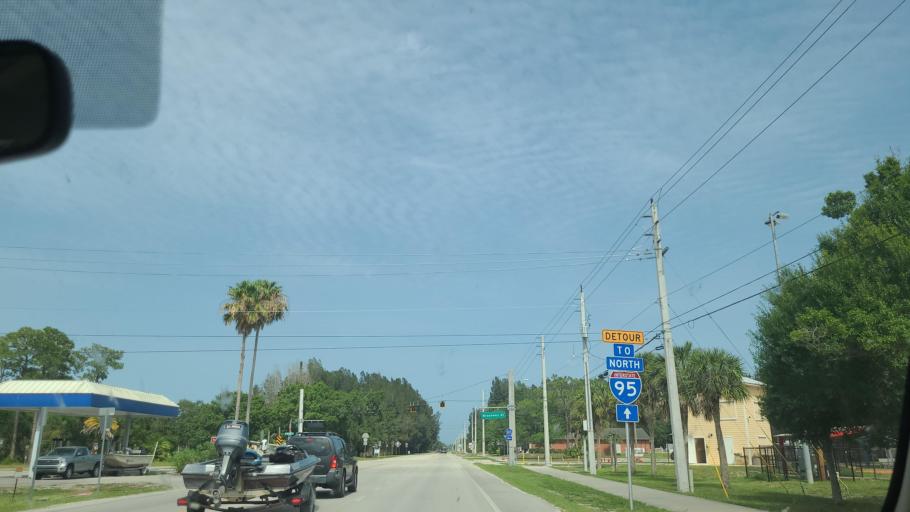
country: US
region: Florida
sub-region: Indian River County
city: Fellsmere
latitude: 27.7677
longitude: -80.6022
